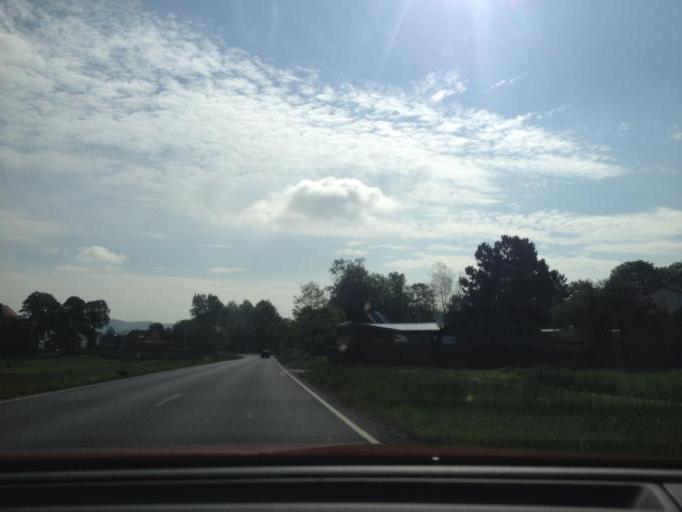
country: DE
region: Bavaria
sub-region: Upper Palatinate
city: Waldershof
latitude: 49.9758
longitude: 12.0553
